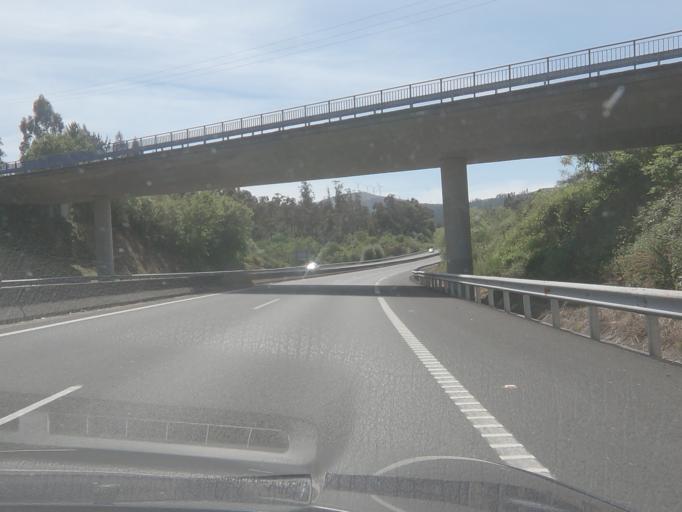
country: ES
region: Galicia
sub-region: Provincia de Pontevedra
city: Valga
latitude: 42.6615
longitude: -8.6369
